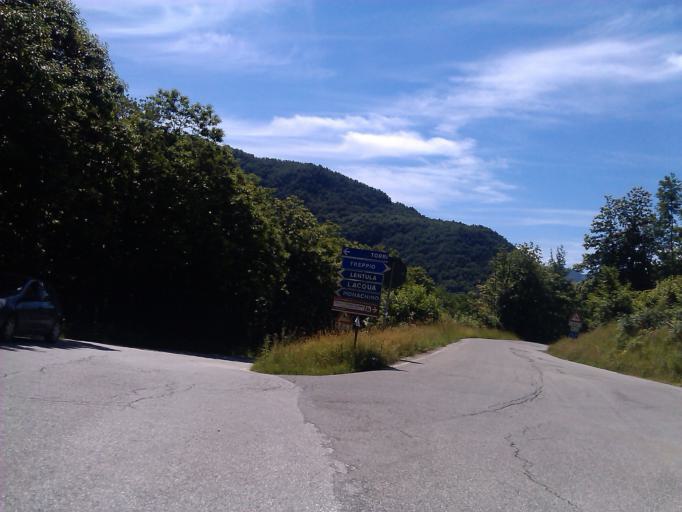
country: IT
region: Tuscany
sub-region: Provincia di Pistoia
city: Sambuca Pistoiese
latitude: 44.0926
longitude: 11.0453
